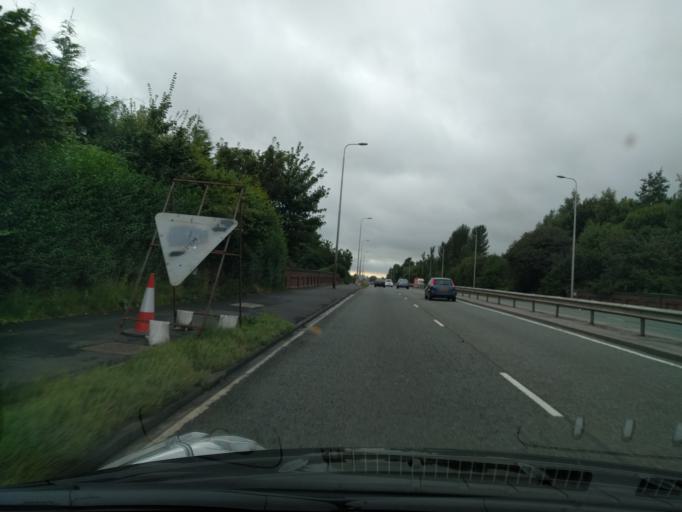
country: GB
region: England
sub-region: Borough of Wigan
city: Ashton in Makerfield
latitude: 53.4725
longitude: -2.6592
